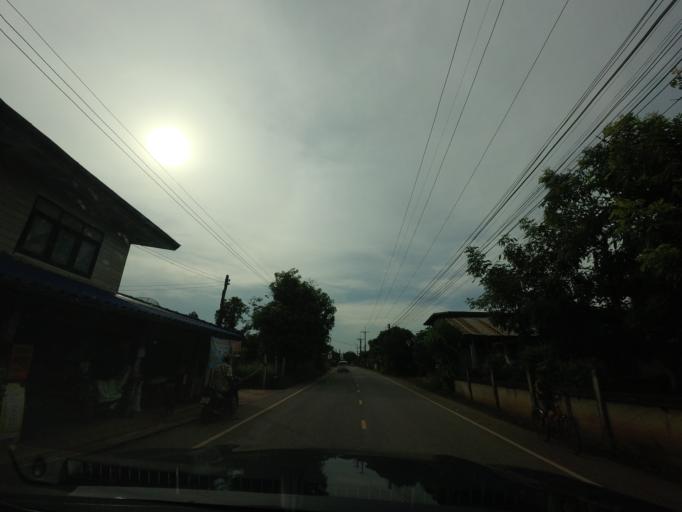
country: TH
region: Changwat Nong Bua Lamphu
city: Na Klang
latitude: 17.3841
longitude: 102.3419
